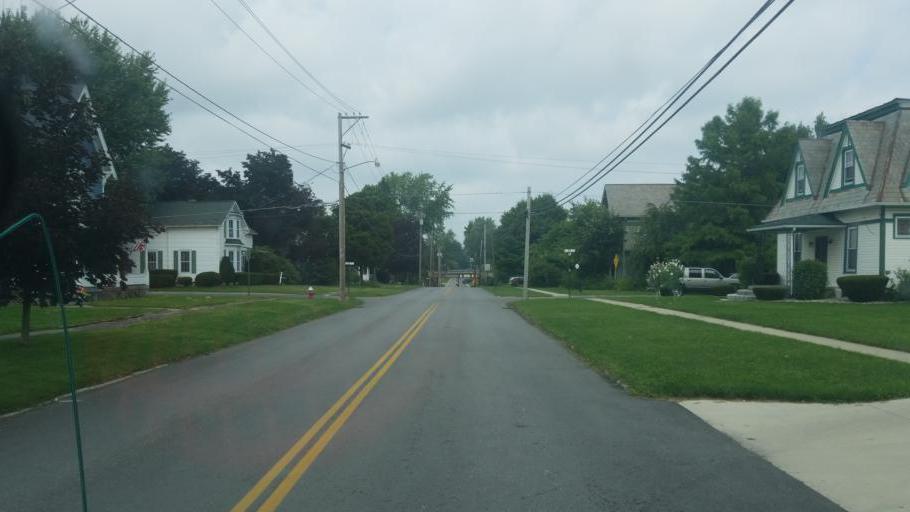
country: US
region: Ohio
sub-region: Huron County
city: Greenwich
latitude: 41.0327
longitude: -82.5165
